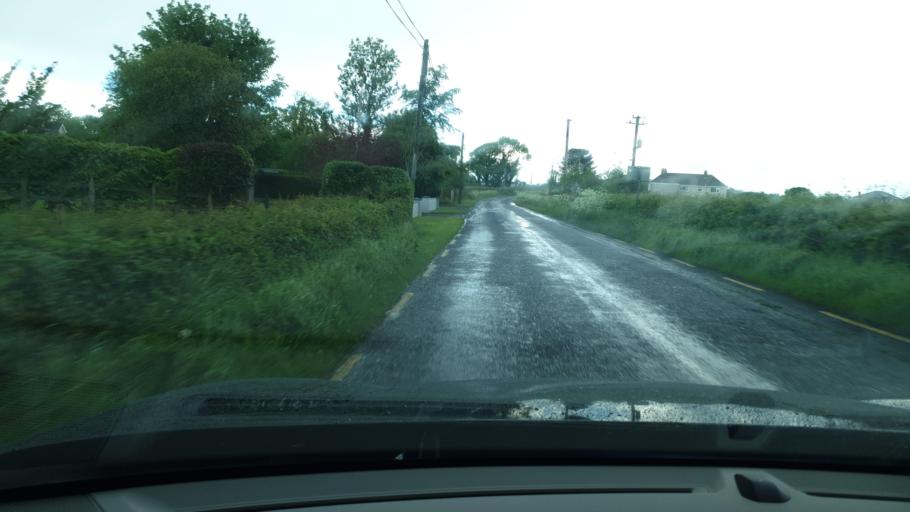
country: IE
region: Leinster
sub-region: Laois
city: Mountmellick
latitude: 53.1085
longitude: -7.3891
